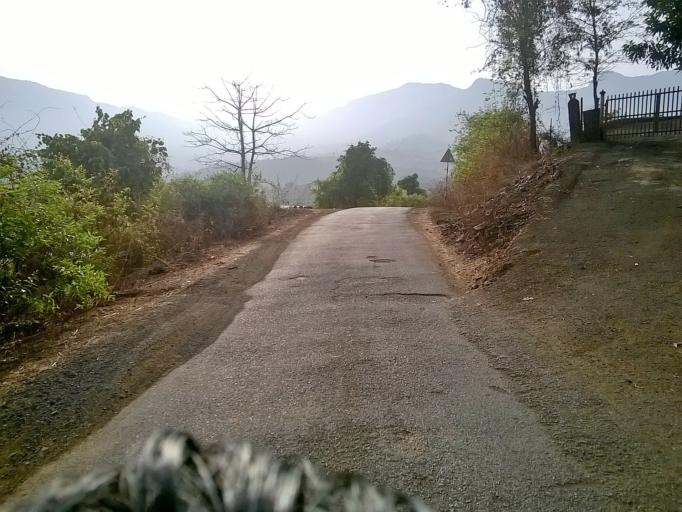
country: IN
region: Maharashtra
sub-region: Raigarh
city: Matheran
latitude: 19.0305
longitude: 73.2450
